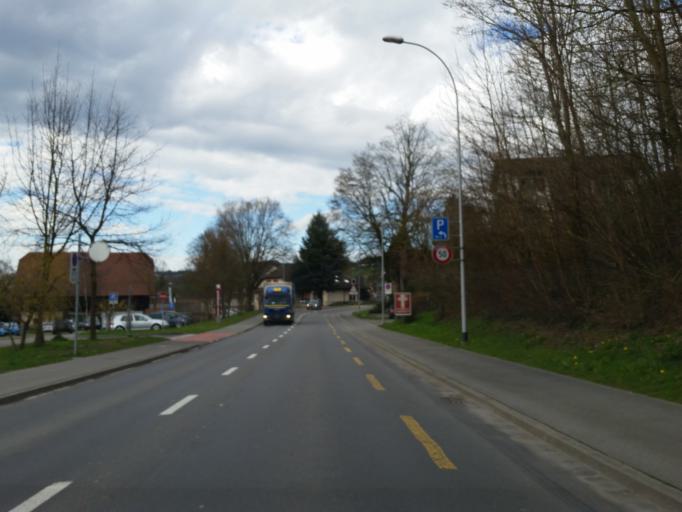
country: CH
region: Lucerne
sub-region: Sursee District
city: Sempach
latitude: 47.1329
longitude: 8.1916
